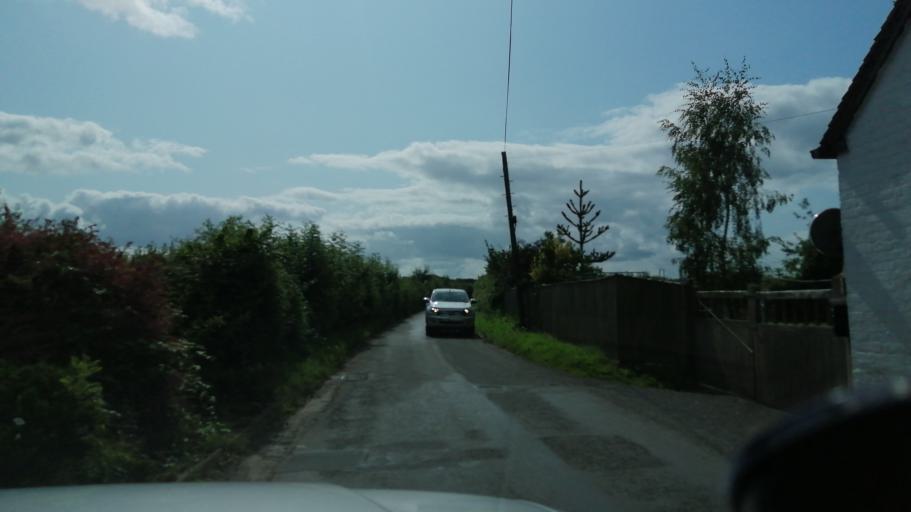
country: GB
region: England
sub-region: Herefordshire
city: Kinnersley
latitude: 52.1329
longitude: -2.9641
